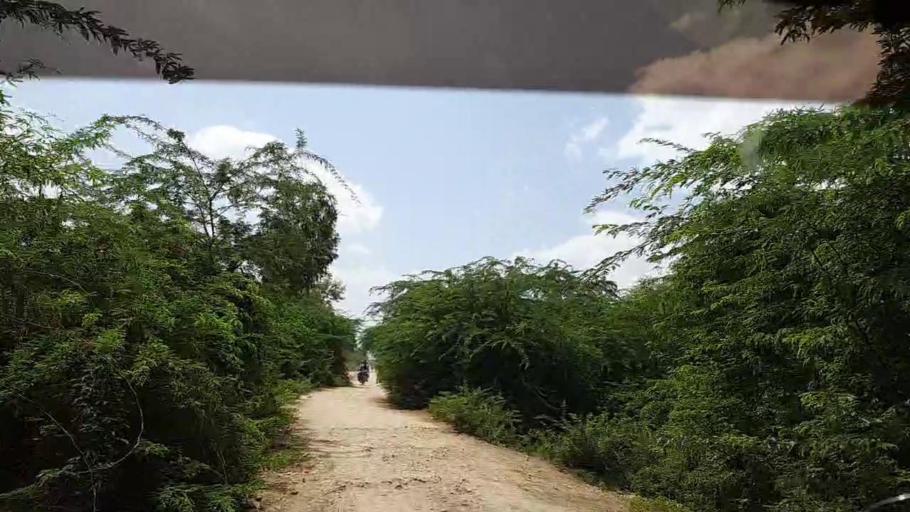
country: PK
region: Sindh
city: Badin
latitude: 24.5830
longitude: 68.7871
